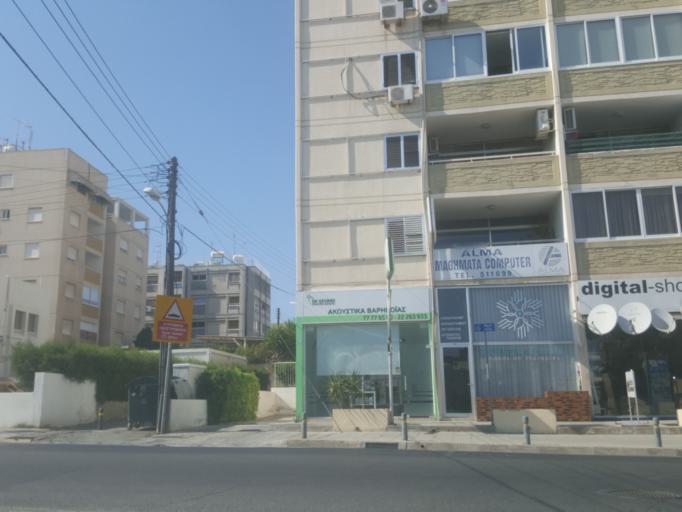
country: CY
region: Lefkosia
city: Nicosia
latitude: 35.1523
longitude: 33.3701
